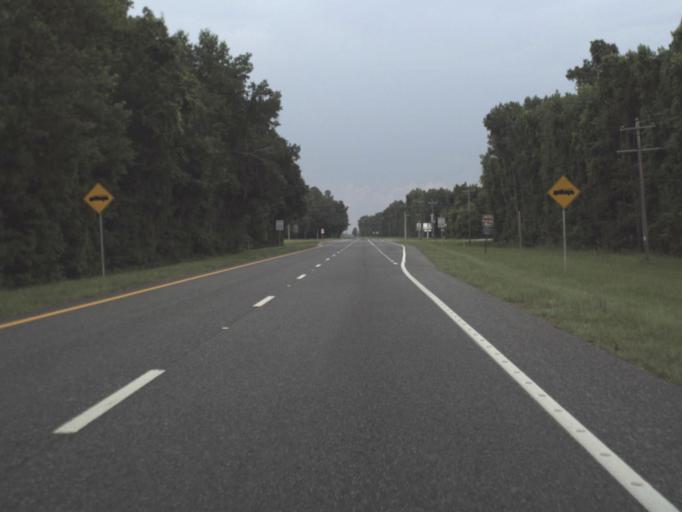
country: US
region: Florida
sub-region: Levy County
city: Williston Highlands
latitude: 29.2556
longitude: -82.7252
